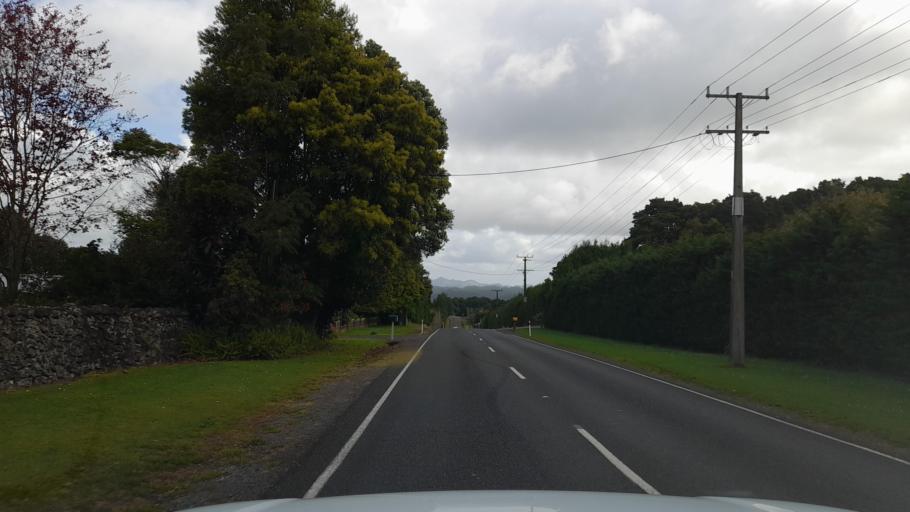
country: NZ
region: Northland
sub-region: Whangarei
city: Maungatapere
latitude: -35.7477
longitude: 174.2543
